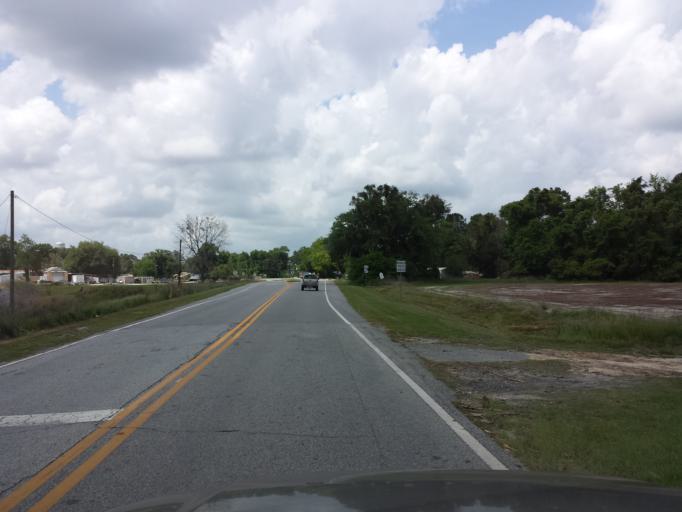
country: US
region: Georgia
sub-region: Echols County
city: Statenville
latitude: 30.6813
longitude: -83.1761
